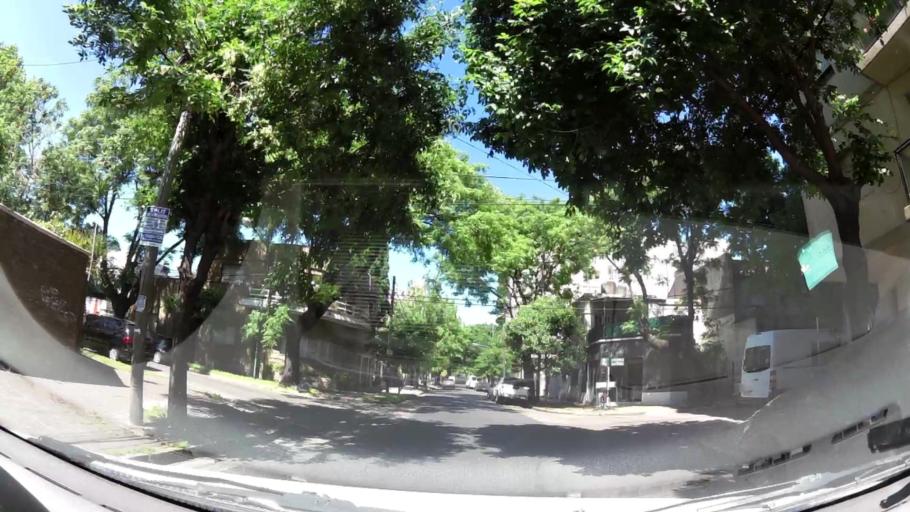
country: AR
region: Buenos Aires
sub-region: Partido de Vicente Lopez
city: Olivos
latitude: -34.5163
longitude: -58.4888
